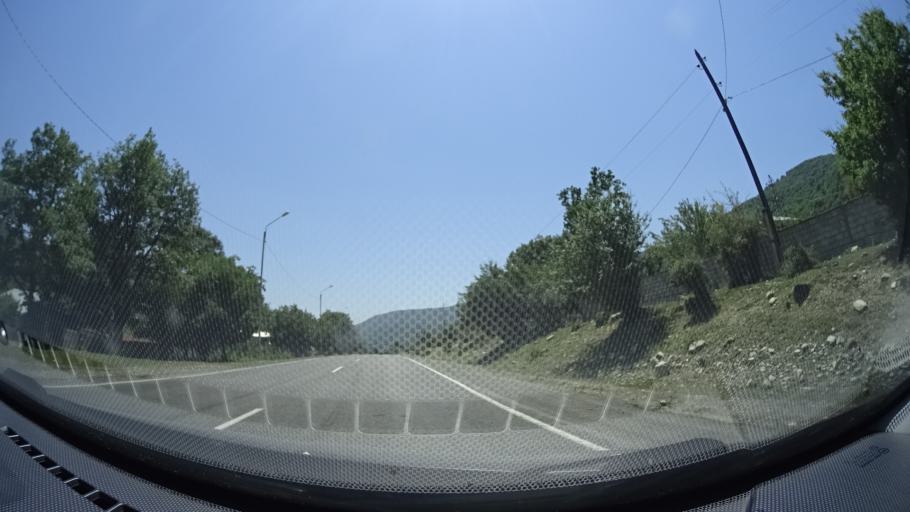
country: GE
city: Zhinvali
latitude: 42.2099
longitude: 44.6740
